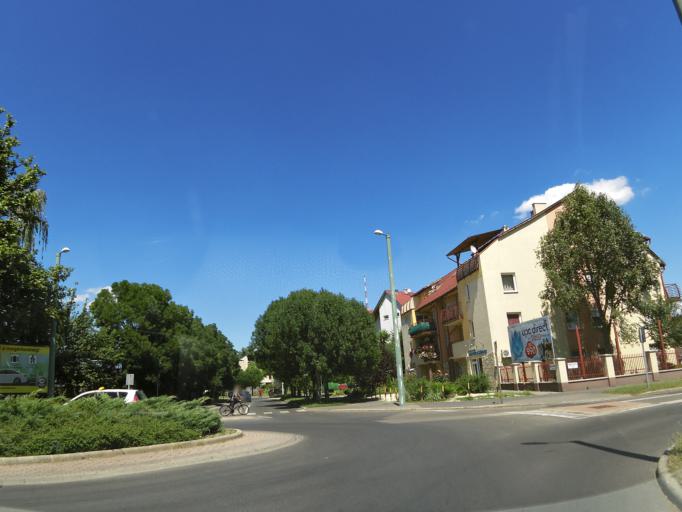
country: HU
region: Csongrad
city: Szeged
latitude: 46.2667
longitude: 20.1390
